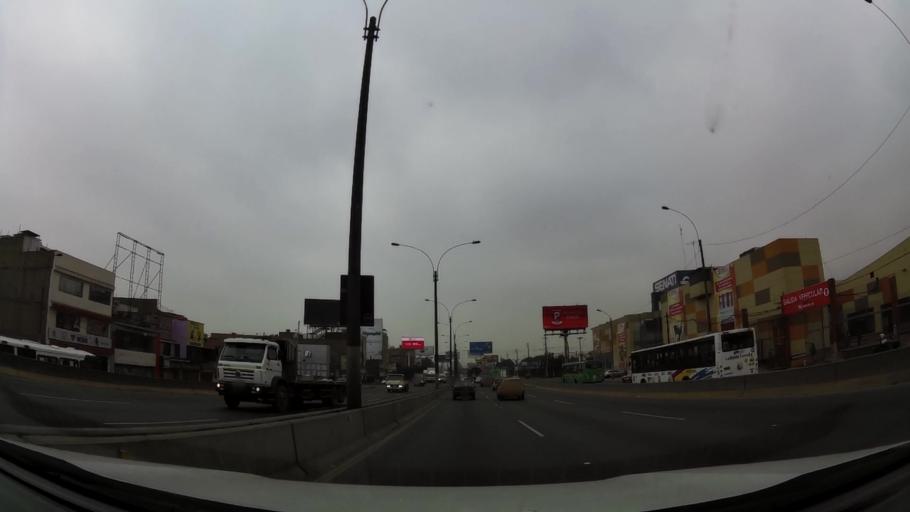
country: PE
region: Lima
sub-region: Lima
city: Independencia
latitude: -12.0018
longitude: -77.0622
